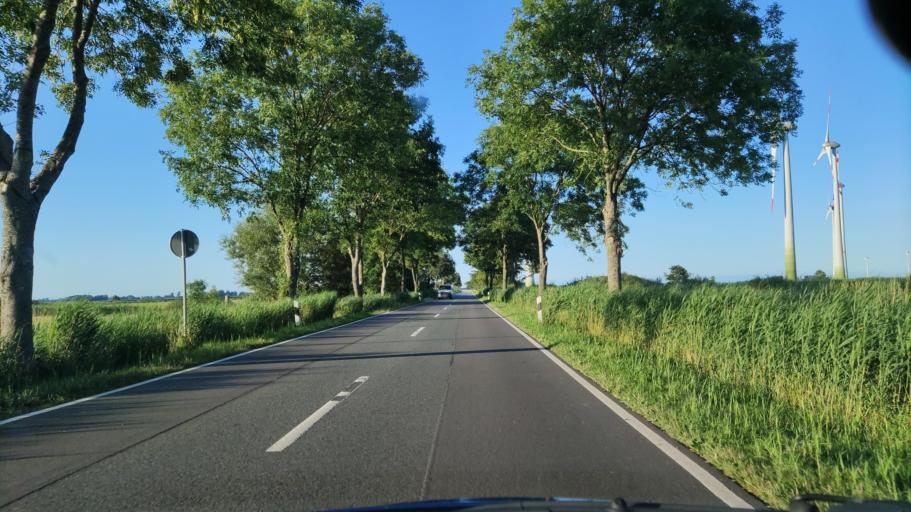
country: DE
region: Lower Saxony
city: Wittmund
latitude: 53.5862
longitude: 7.8002
